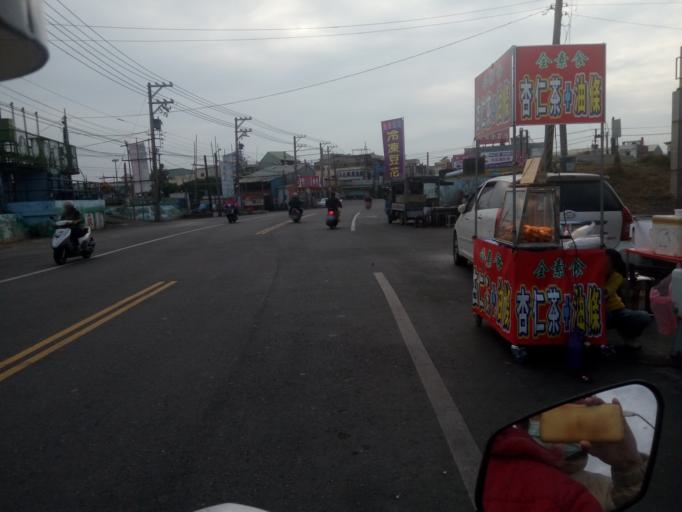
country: TW
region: Taiwan
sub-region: Chiayi
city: Taibao
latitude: 23.4996
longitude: 120.3680
